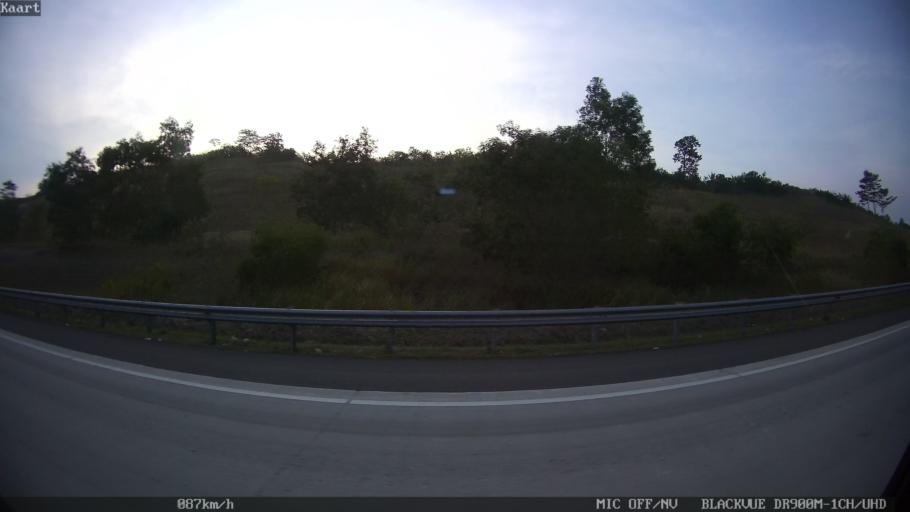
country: ID
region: Lampung
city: Penengahan
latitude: -5.8251
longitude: 105.7343
